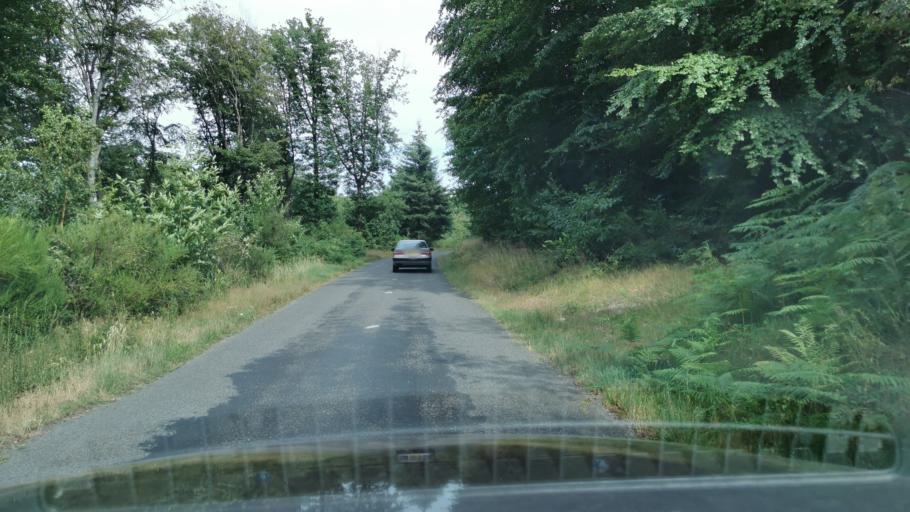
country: FR
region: Bourgogne
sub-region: Departement de Saone-et-Loire
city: Marmagne
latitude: 46.8064
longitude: 4.2912
